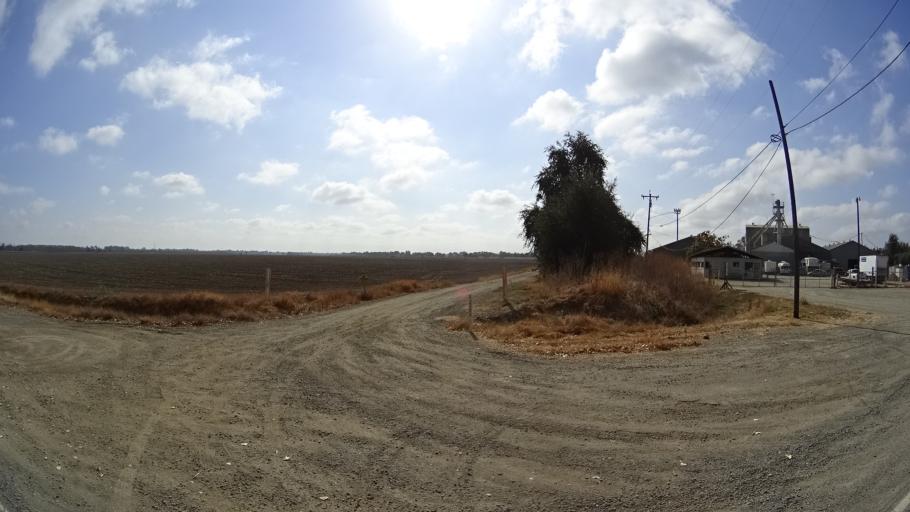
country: US
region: California
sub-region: Yolo County
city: Woodland
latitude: 38.7958
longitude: -121.7190
